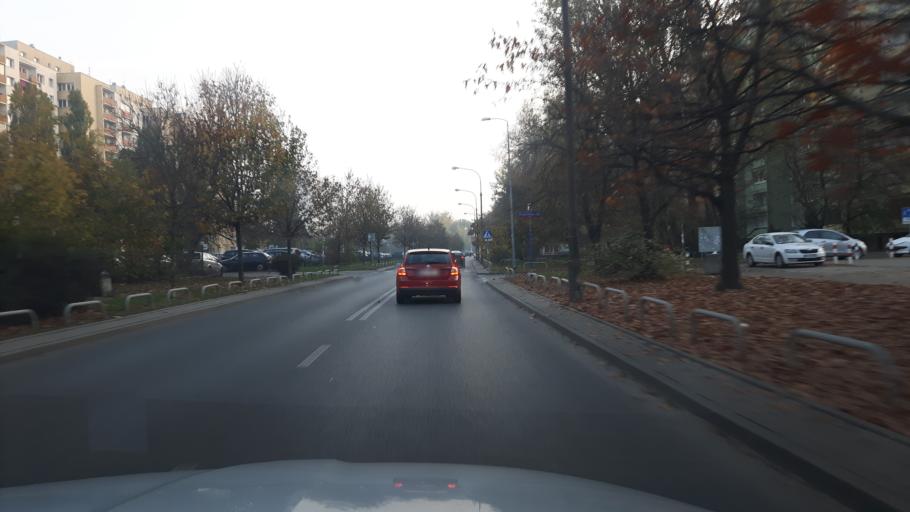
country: PL
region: Masovian Voivodeship
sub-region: Warszawa
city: Mokotow
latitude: 52.1779
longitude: 21.0138
